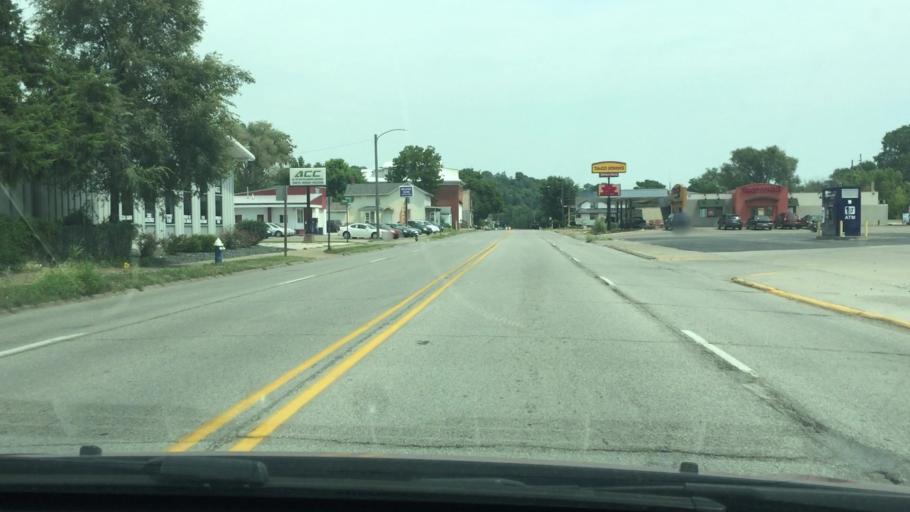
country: US
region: Iowa
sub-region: Muscatine County
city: Muscatine
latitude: 41.4097
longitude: -91.0625
